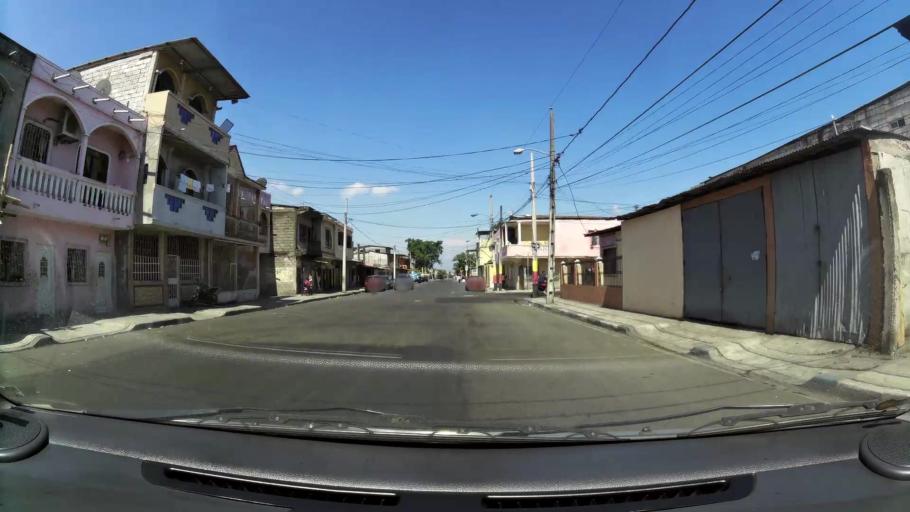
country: EC
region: Guayas
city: Guayaquil
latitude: -2.2248
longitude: -79.9345
